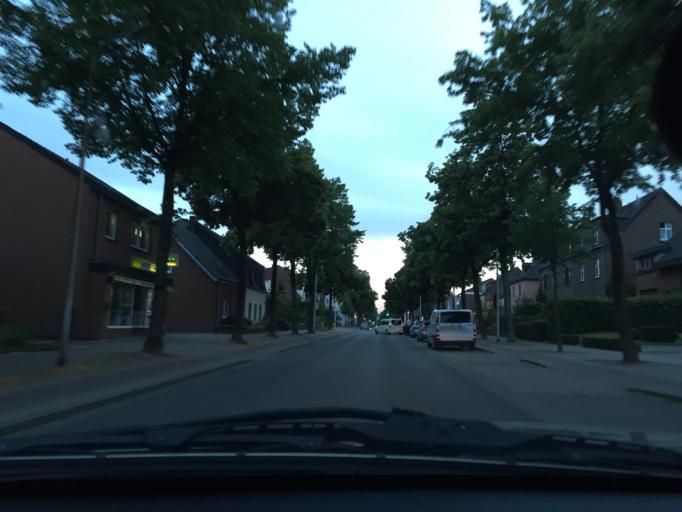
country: DE
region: North Rhine-Westphalia
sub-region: Regierungsbezirk Dusseldorf
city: Kleve
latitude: 51.7779
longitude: 6.1238
